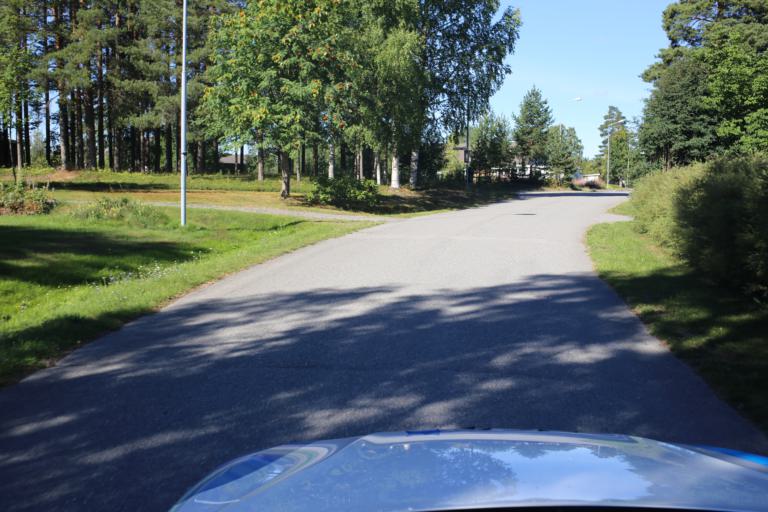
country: SE
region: Vaesterbotten
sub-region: Skelleftea Kommun
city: Viken
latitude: 64.7461
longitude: 20.7715
